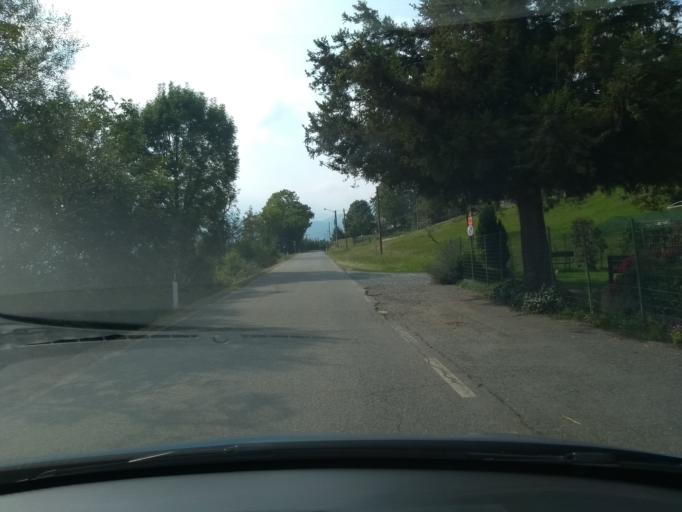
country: IT
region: Piedmont
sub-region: Provincia di Torino
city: Lanzo Torinese
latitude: 45.3011
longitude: 7.4967
